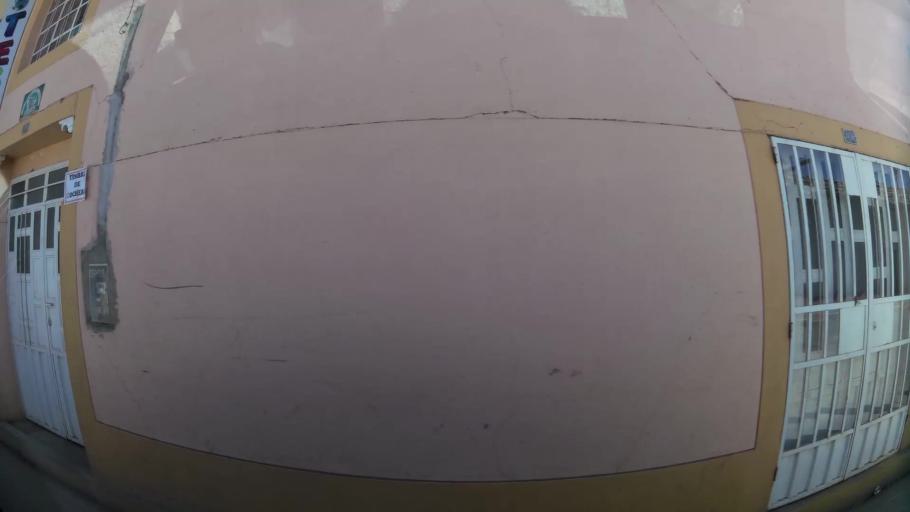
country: PE
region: Junin
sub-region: Provincia de Concepcion
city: Concepcion
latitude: -11.9152
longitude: -75.3190
